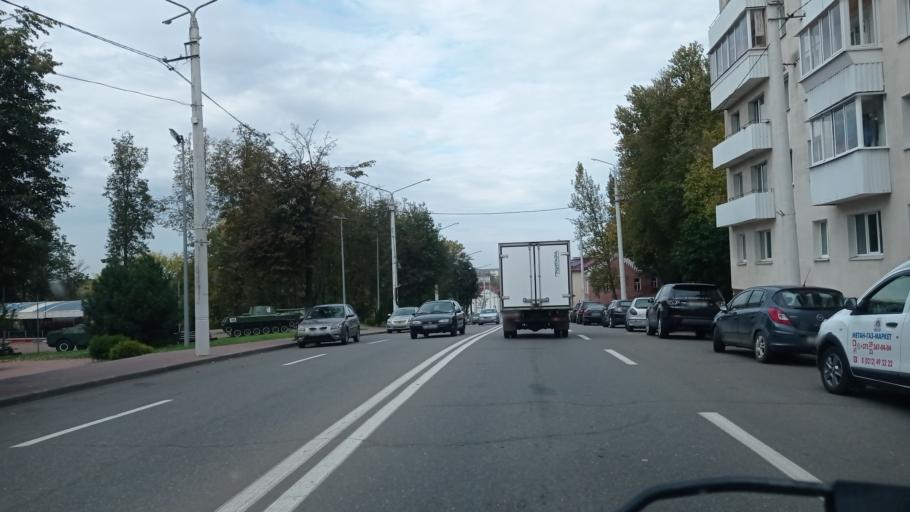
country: BY
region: Vitebsk
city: Vitebsk
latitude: 55.1853
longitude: 30.2027
